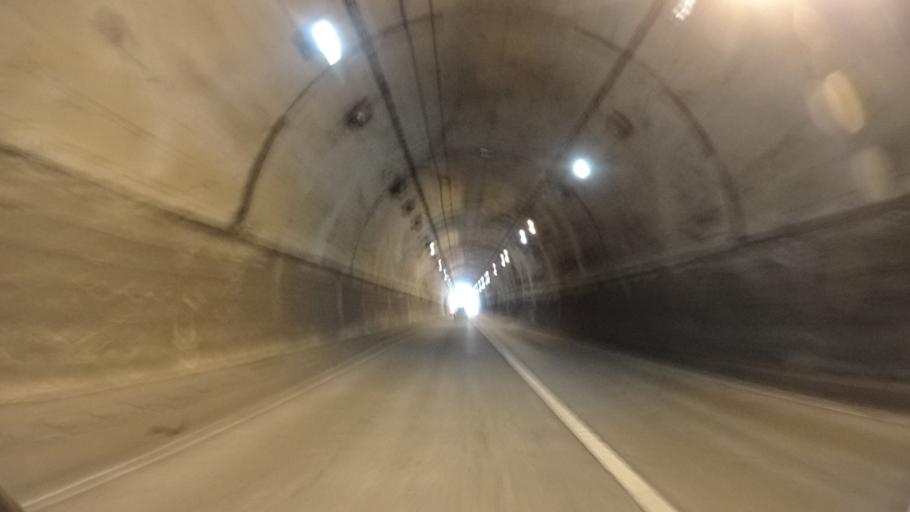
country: JP
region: Ehime
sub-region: Nishiuwa-gun
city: Ikata-cho
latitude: 33.4860
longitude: 132.3357
